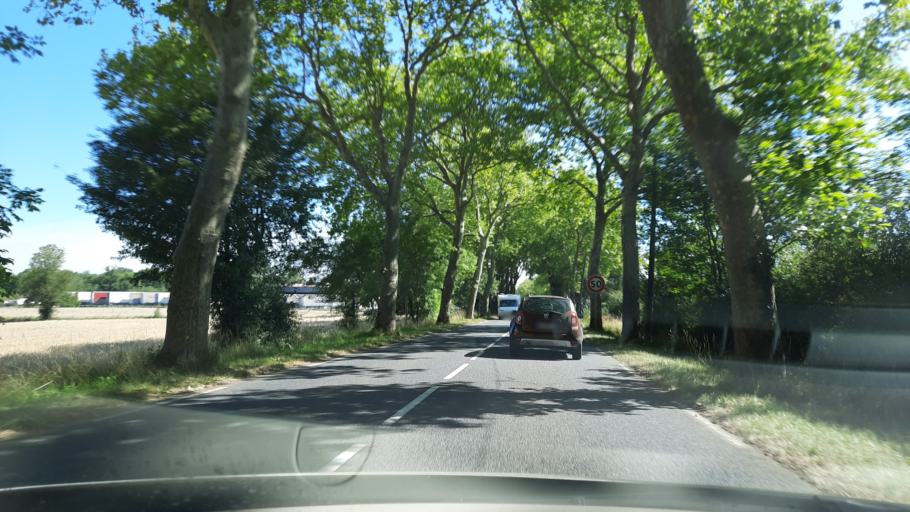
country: FR
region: Midi-Pyrenees
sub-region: Departement du Tarn-et-Garonne
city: Caylus
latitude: 44.3160
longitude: 1.8907
